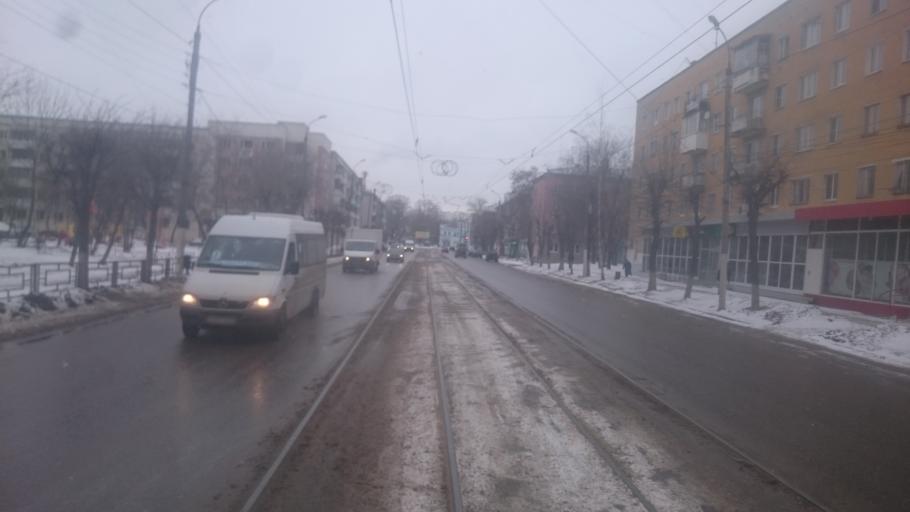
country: RU
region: Tverskaya
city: Tver
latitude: 56.8701
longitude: 35.8846
